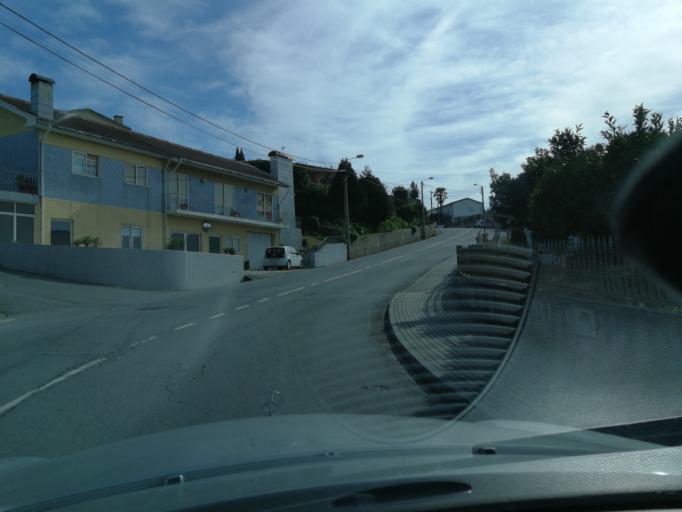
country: PT
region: Braga
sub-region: Vila Nova de Famalicao
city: Vila Nova de Famalicao
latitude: 41.4278
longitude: -8.5204
